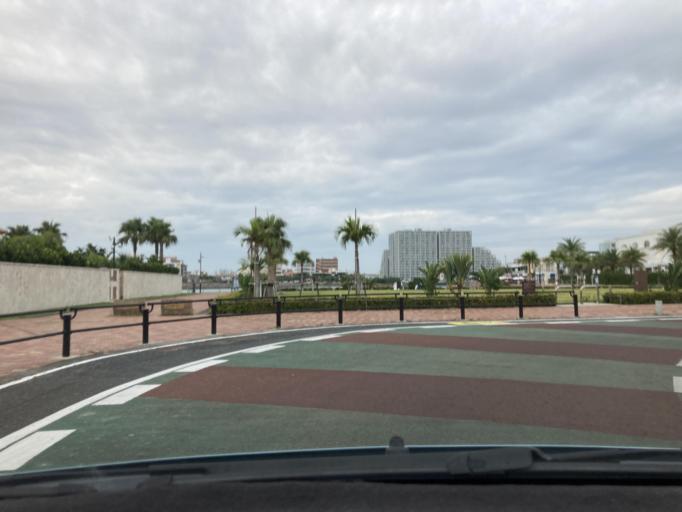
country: JP
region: Okinawa
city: Chatan
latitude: 26.3181
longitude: 127.7538
